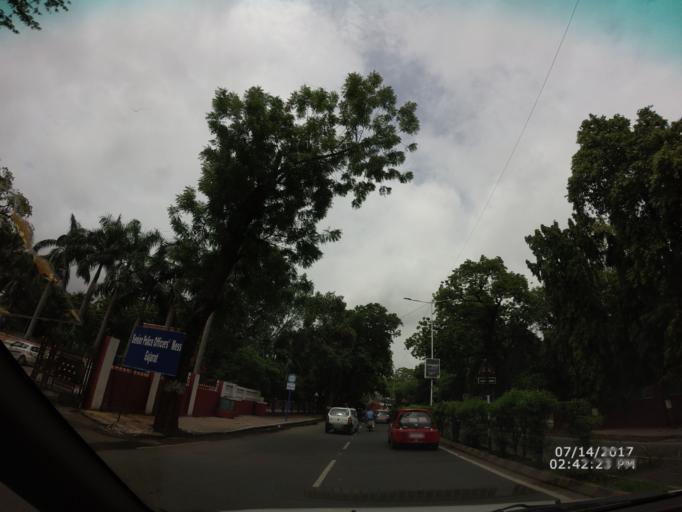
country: IN
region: Gujarat
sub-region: Ahmadabad
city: Ahmedabad
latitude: 23.0635
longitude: 72.5982
